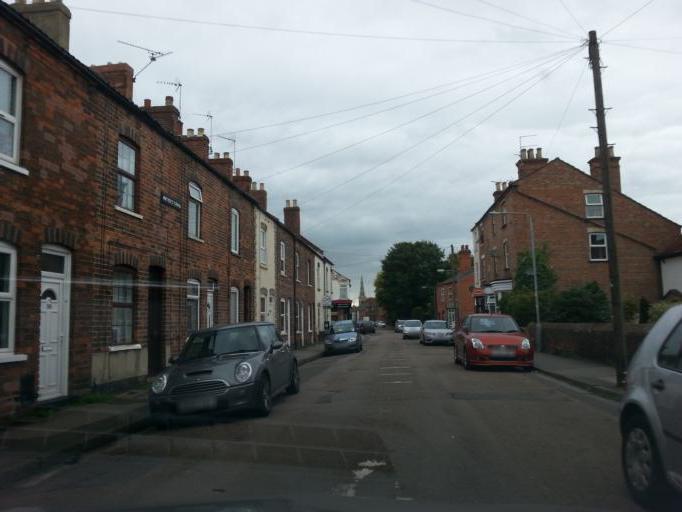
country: GB
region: England
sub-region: Nottinghamshire
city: Newark on Trent
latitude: 53.0729
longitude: -0.7977
